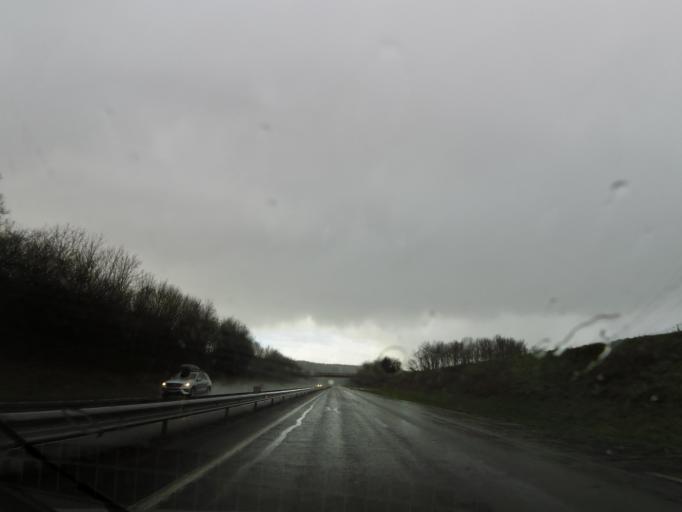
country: FR
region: Bourgogne
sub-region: Departement de Saone-et-Loire
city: Sance
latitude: 46.3433
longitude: 4.8363
